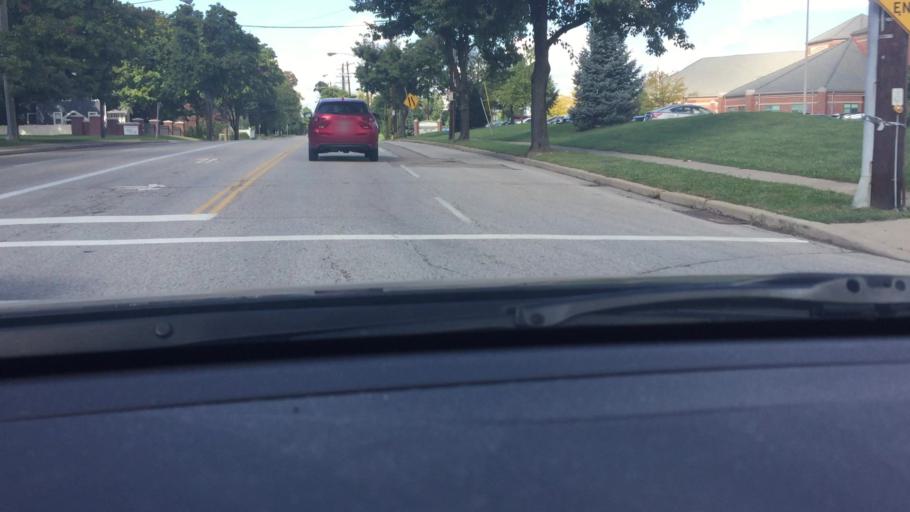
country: US
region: Ohio
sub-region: Hamilton County
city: Fairfax
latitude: 39.1647
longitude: -84.4078
